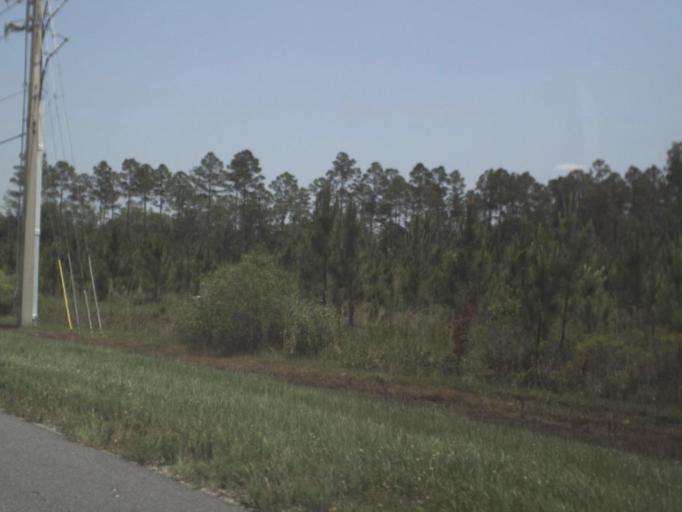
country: US
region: Florida
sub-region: Duval County
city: Baldwin
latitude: 30.2088
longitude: -81.9611
